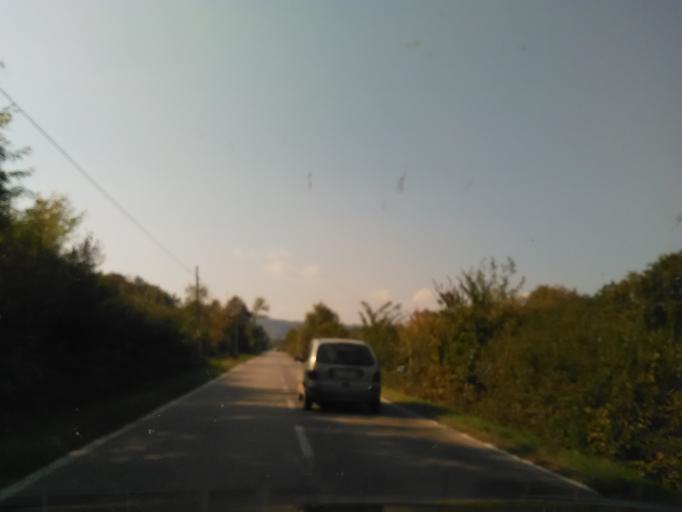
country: IT
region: Piedmont
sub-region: Provincia di Biella
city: Salussola
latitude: 45.4327
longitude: 8.1218
